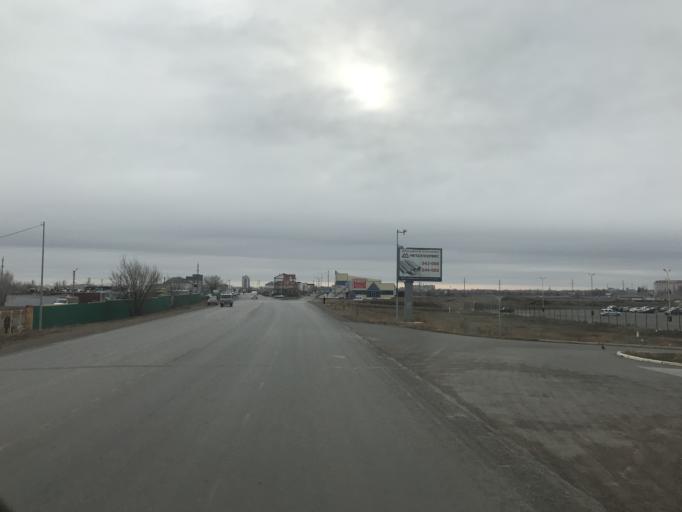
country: KZ
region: Batys Qazaqstan
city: Oral
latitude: 51.2665
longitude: 51.4063
